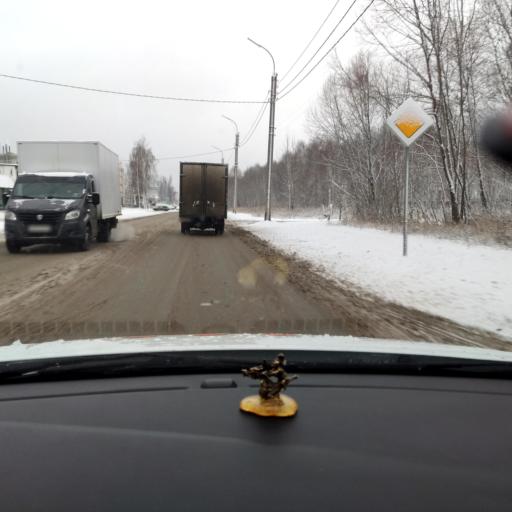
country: RU
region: Tatarstan
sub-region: Zelenodol'skiy Rayon
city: Zelenodolsk
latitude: 55.8638
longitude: 48.5488
